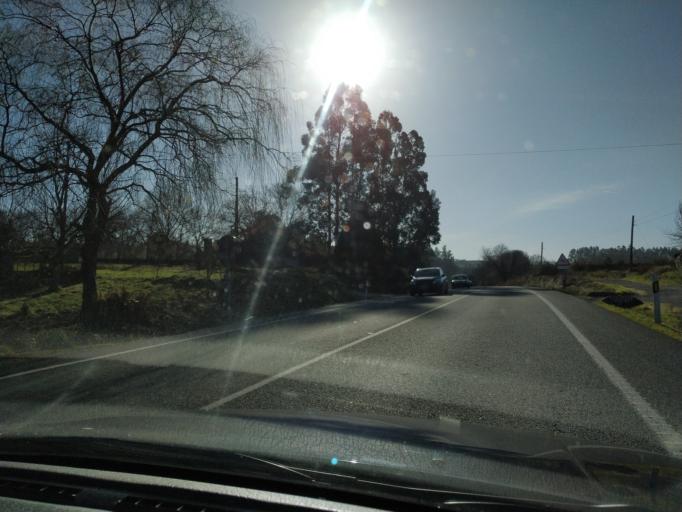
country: ES
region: Galicia
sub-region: Provincia da Coruna
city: Vedra
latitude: 42.8092
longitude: -8.4794
